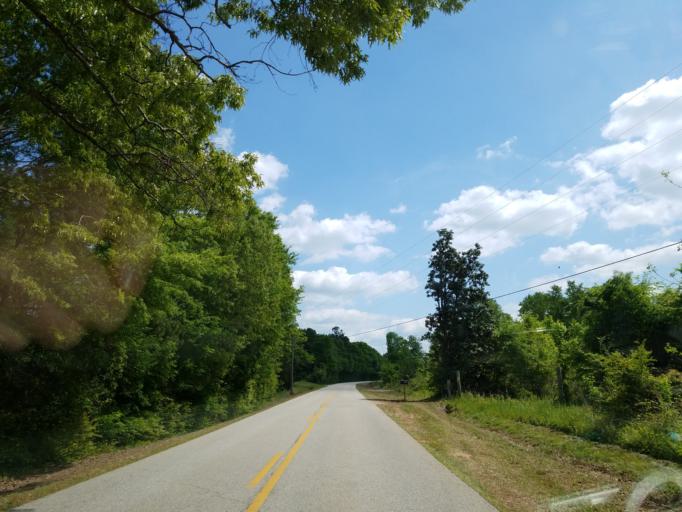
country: US
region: Georgia
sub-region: Monroe County
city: Forsyth
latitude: 33.0991
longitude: -83.9650
